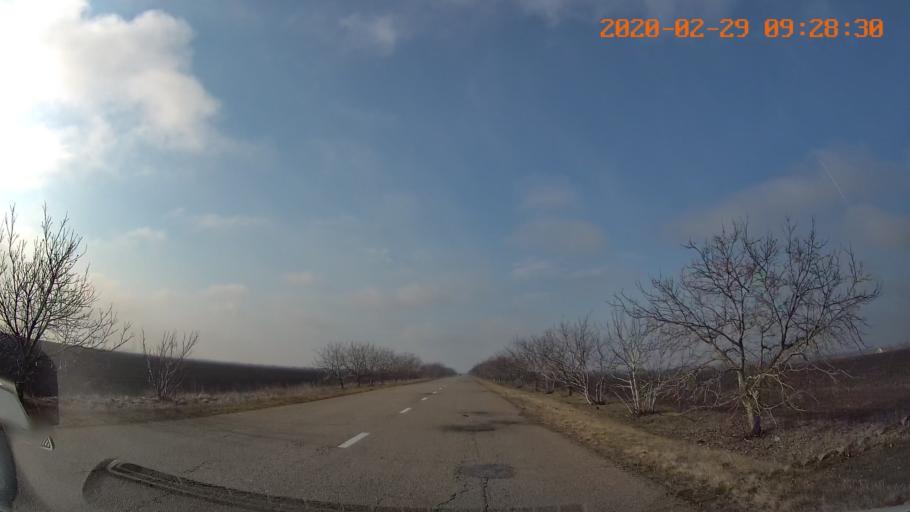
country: UA
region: Odessa
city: Lymanske
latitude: 46.6883
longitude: 29.9290
